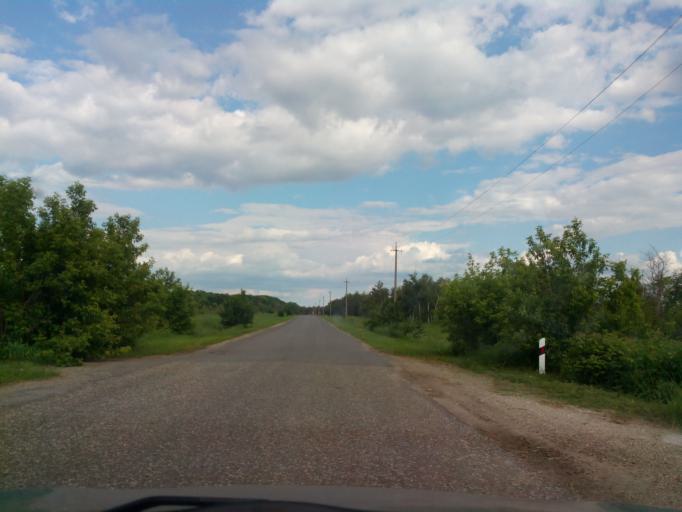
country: RU
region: Volgograd
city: Slashchevskaya
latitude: 49.7957
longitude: 42.3752
